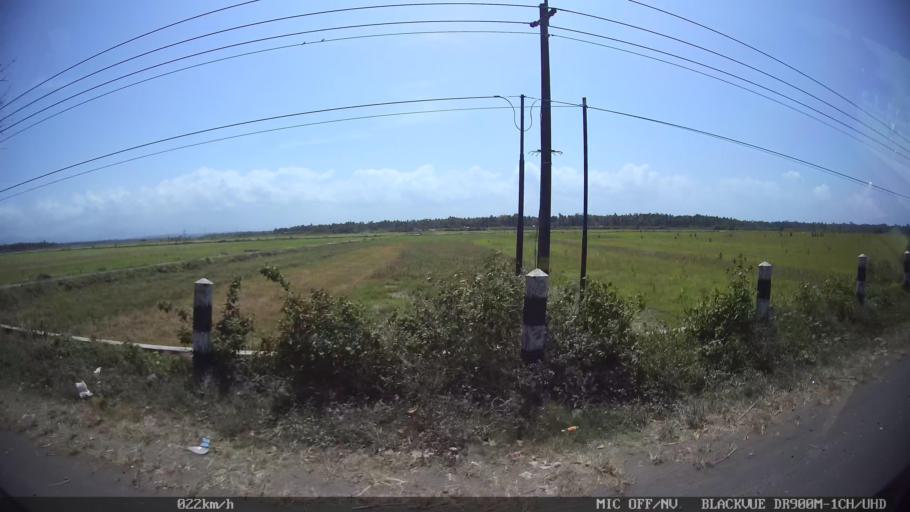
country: ID
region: Daerah Istimewa Yogyakarta
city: Srandakan
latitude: -7.9479
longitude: 110.1811
